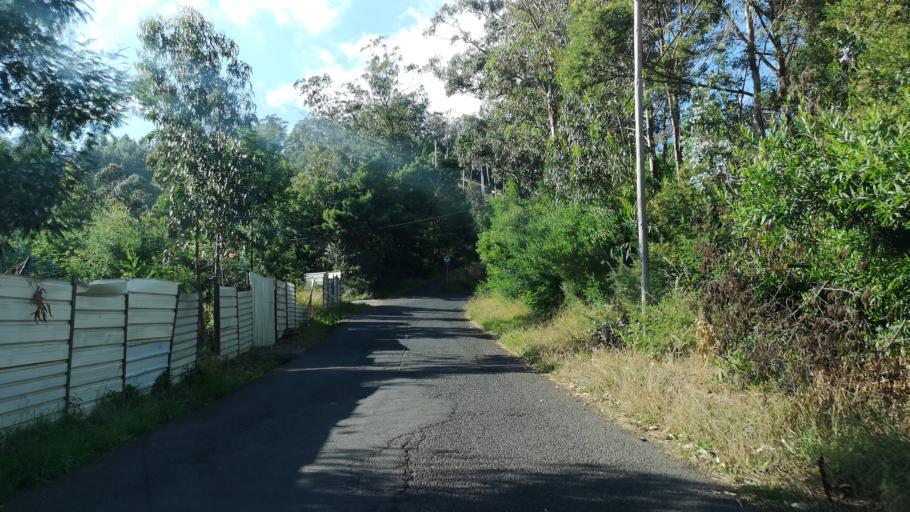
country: PT
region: Madeira
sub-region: Santa Cruz
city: Camacha
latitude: 32.6634
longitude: -16.8370
